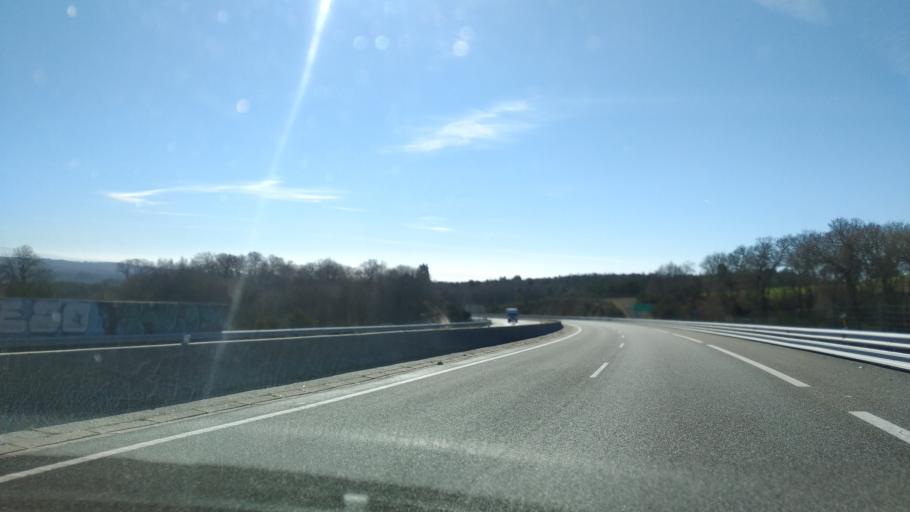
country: ES
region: Galicia
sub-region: Provincia de Pontevedra
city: Dozon
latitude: 42.5439
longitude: -8.0205
